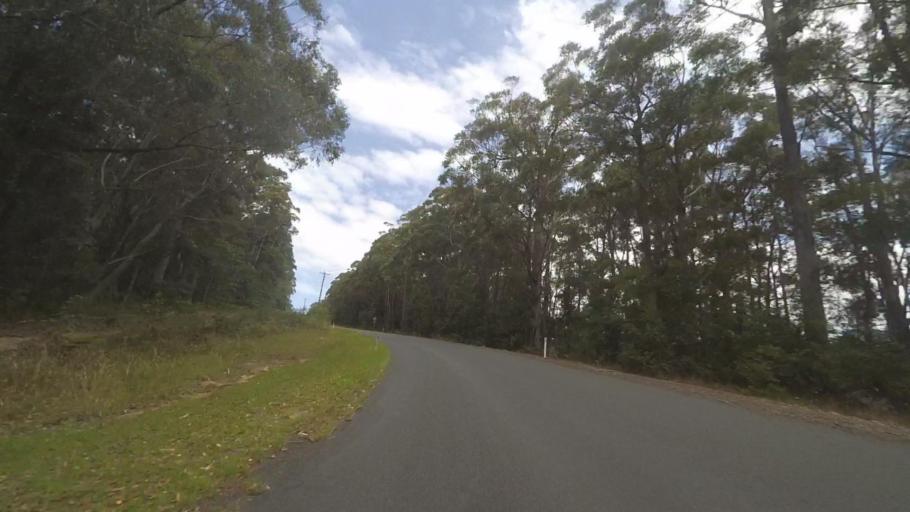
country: AU
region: New South Wales
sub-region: Shoalhaven Shire
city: Milton
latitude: -35.3844
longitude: 150.3654
